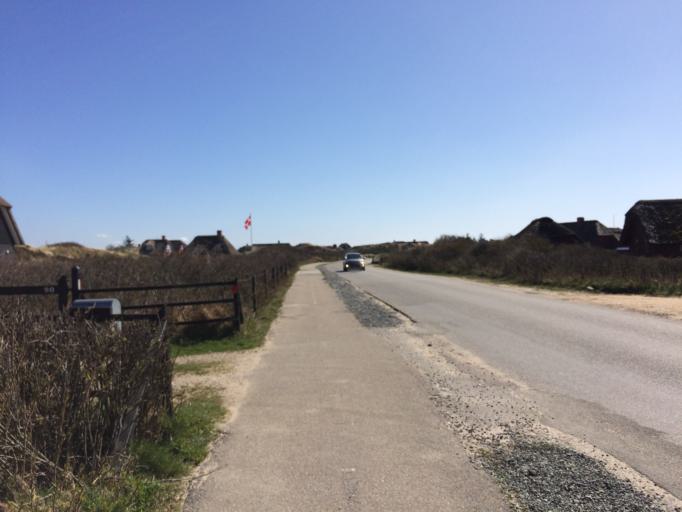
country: DK
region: South Denmark
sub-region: Varde Kommune
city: Oksbol
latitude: 55.5570
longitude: 8.0883
